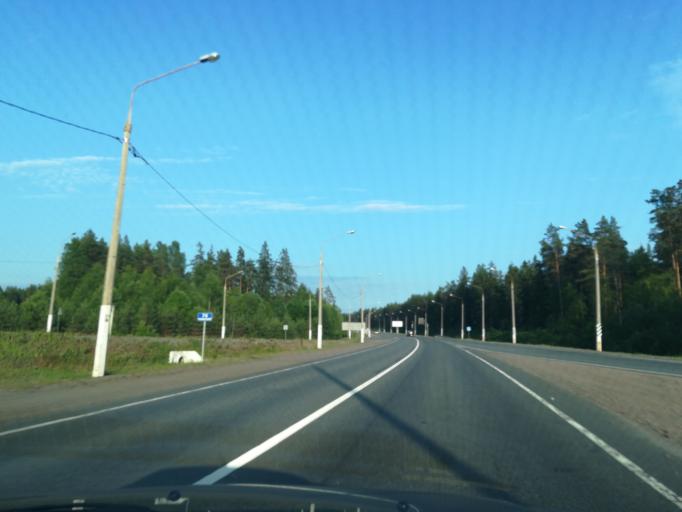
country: RU
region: Leningrad
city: Vyborg
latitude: 60.6734
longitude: 28.8744
